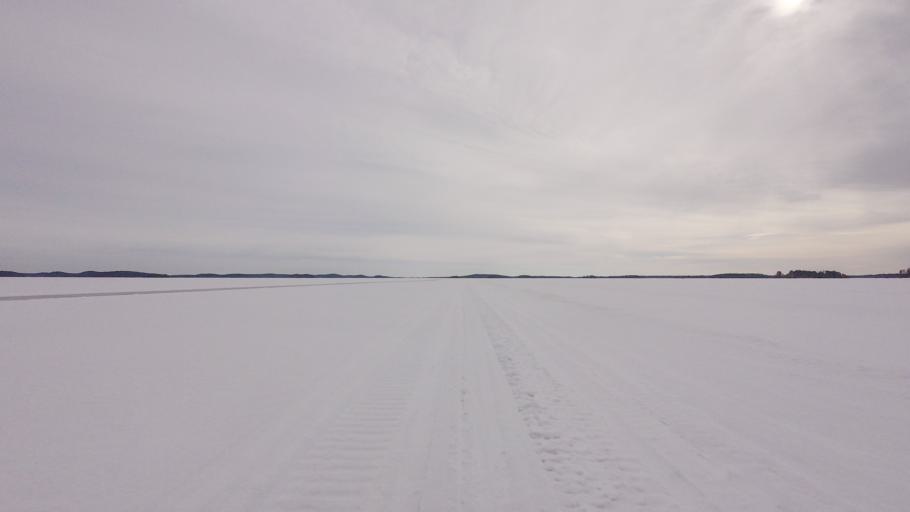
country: FI
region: Southern Savonia
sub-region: Savonlinna
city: Rantasalmi
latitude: 62.1127
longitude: 28.3804
